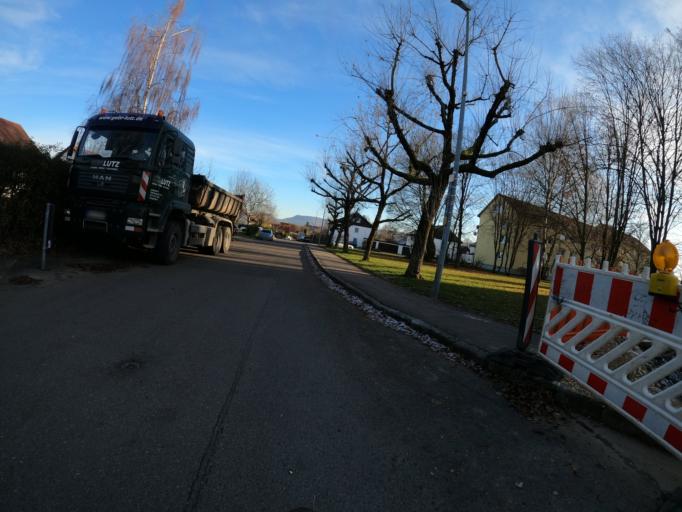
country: DE
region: Baden-Wuerttemberg
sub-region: Regierungsbezirk Stuttgart
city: Boll
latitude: 48.6730
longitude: 9.6072
